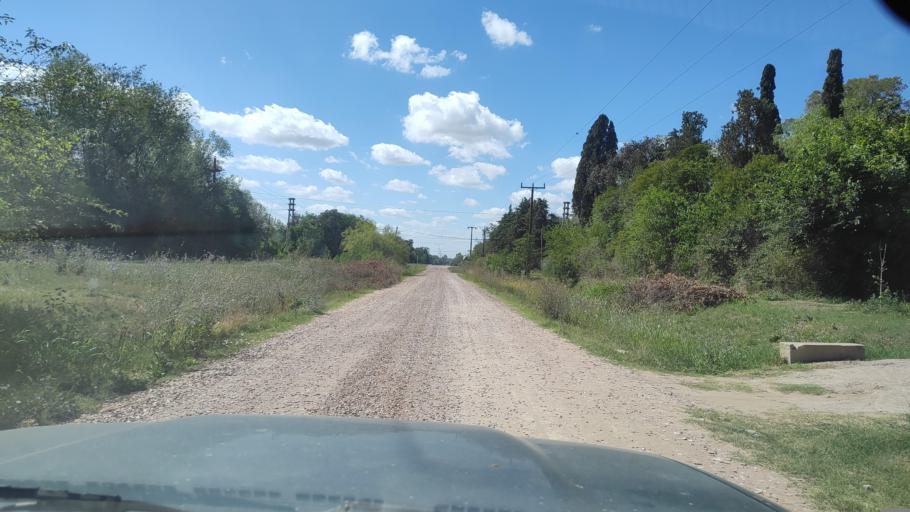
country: AR
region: Buenos Aires
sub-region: Partido de Lujan
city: Lujan
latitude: -34.5475
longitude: -59.1380
